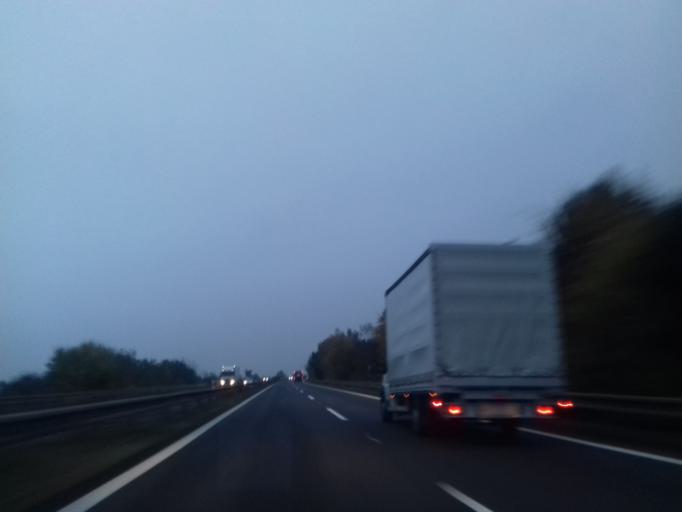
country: CZ
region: Olomoucky
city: Prikazy
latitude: 49.6367
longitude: 17.1470
